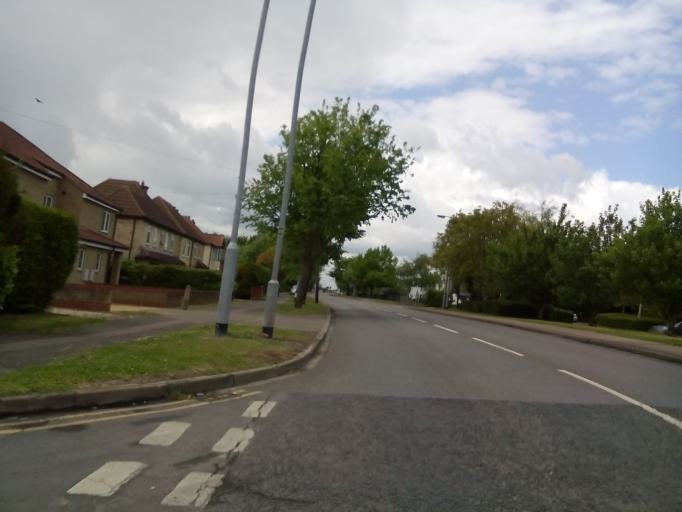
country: GB
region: England
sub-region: Cambridgeshire
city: Fulbourn
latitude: 52.1937
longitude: 0.1742
